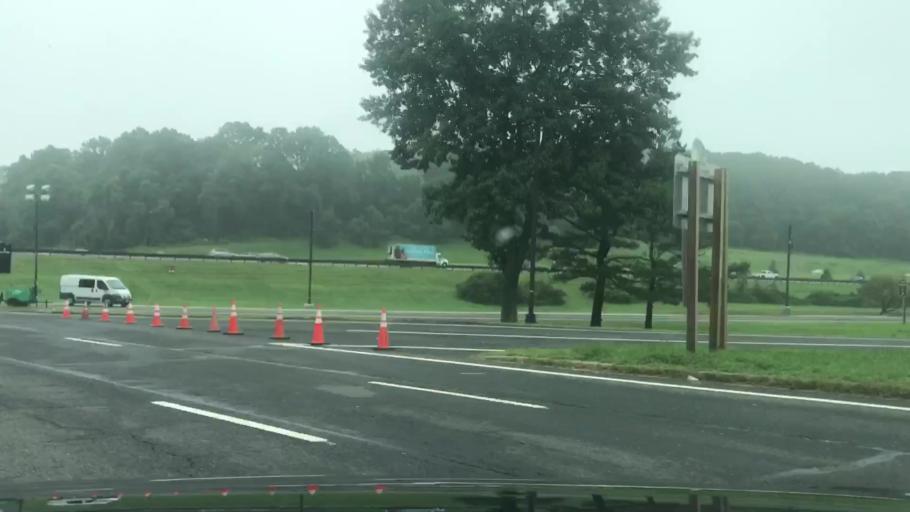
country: US
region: New Jersey
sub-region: Monmouth County
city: Strathmore
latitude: 40.3903
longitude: -74.1774
